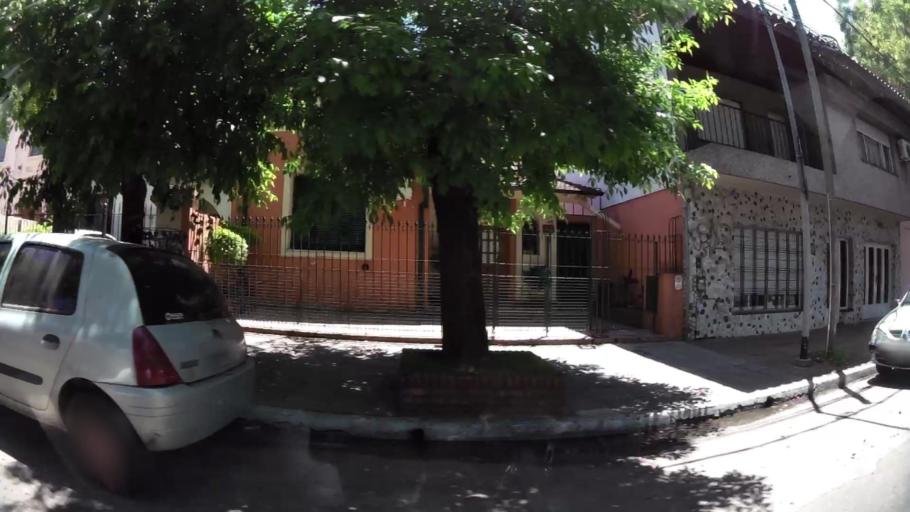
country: AR
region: Buenos Aires
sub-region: Partido de General San Martin
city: General San Martin
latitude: -34.5805
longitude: -58.5366
